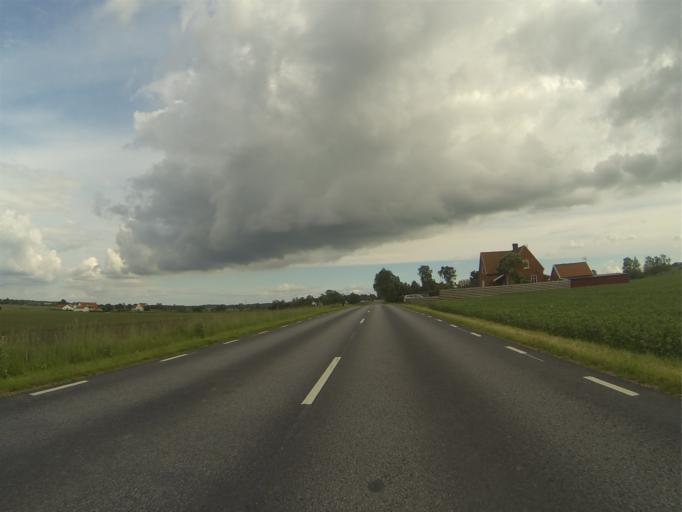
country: SE
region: Skane
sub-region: Eslovs Kommun
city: Eslov
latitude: 55.7437
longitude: 13.3277
